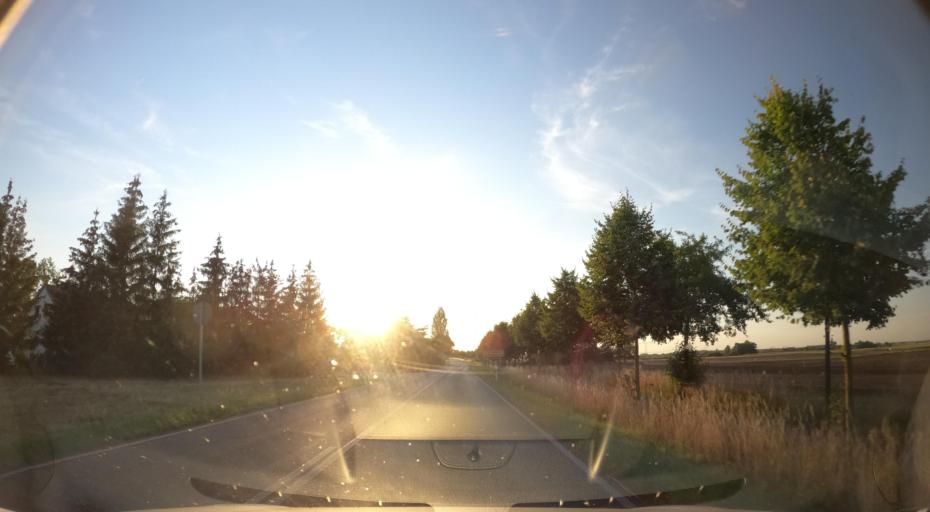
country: DE
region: Mecklenburg-Vorpommern
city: Viereck
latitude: 53.5027
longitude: 14.0434
